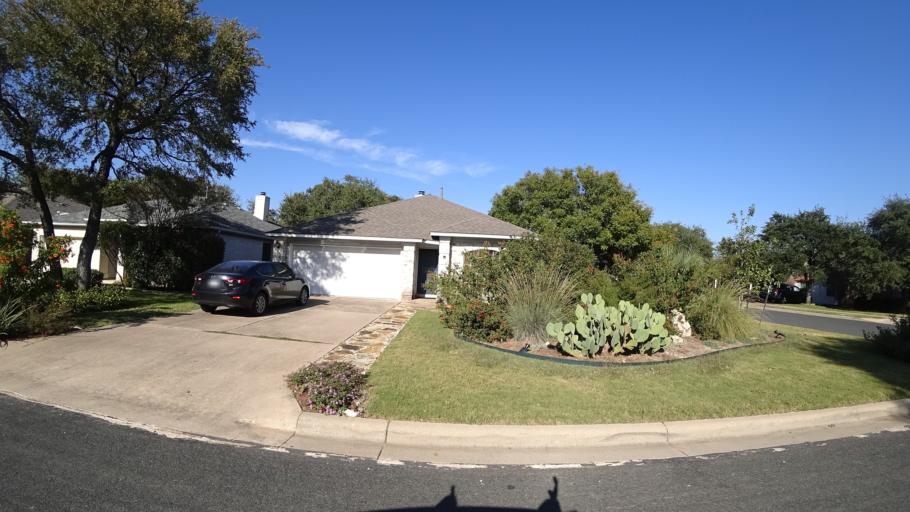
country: US
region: Texas
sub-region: Travis County
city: Shady Hollow
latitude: 30.2089
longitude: -97.8555
